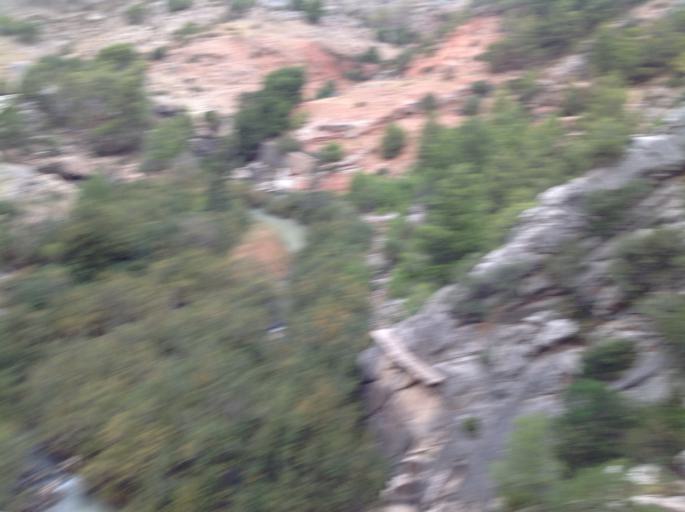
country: ES
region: Andalusia
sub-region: Provincia de Malaga
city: Ardales
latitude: 36.9317
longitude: -4.7874
